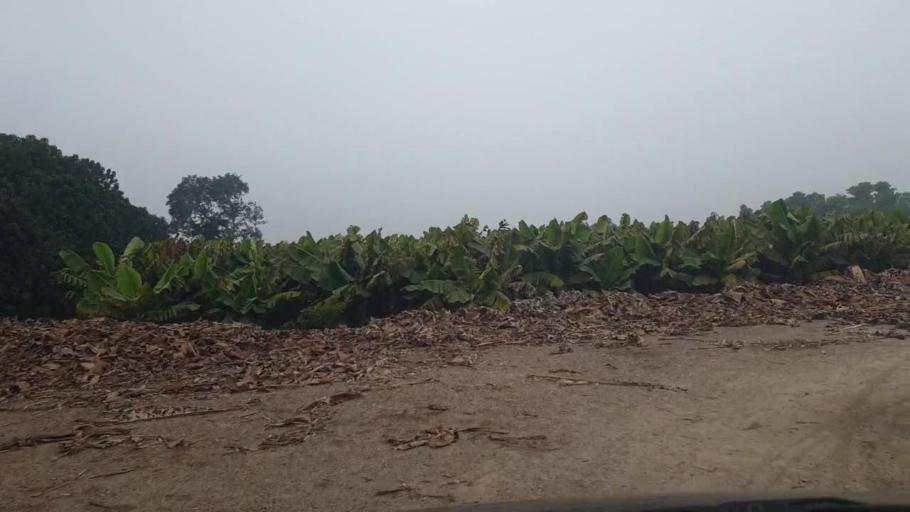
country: PK
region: Sindh
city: Tando Adam
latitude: 25.8057
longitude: 68.6656
